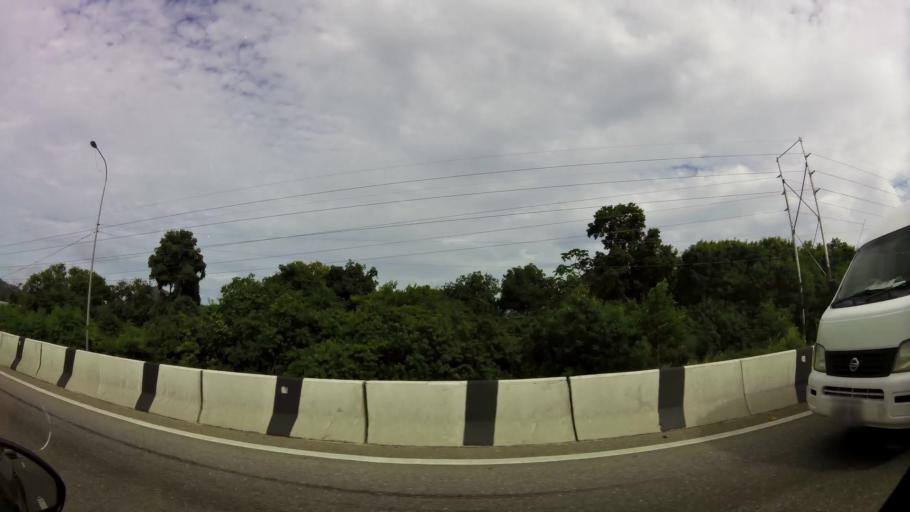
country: TT
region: City of Port of Spain
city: Mucurapo
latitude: 10.6655
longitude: -61.5363
